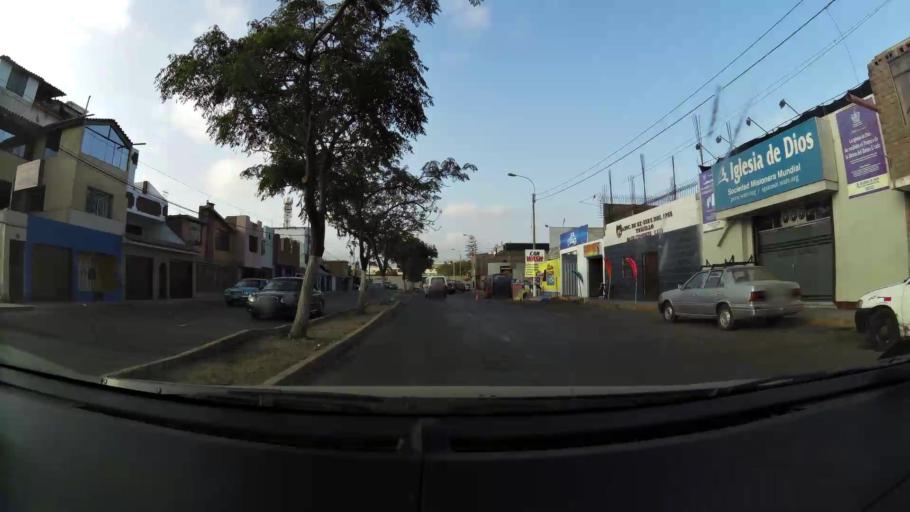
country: PE
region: La Libertad
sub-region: Provincia de Trujillo
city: El Porvenir
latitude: -8.0975
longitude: -79.0121
